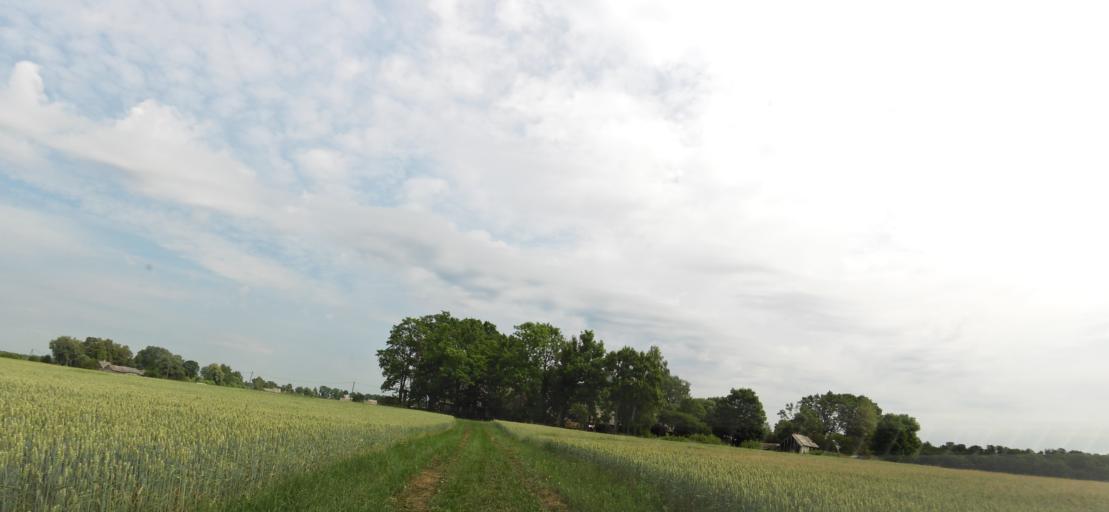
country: LT
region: Panevezys
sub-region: Birzai
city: Birzai
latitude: 56.3203
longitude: 24.6988
